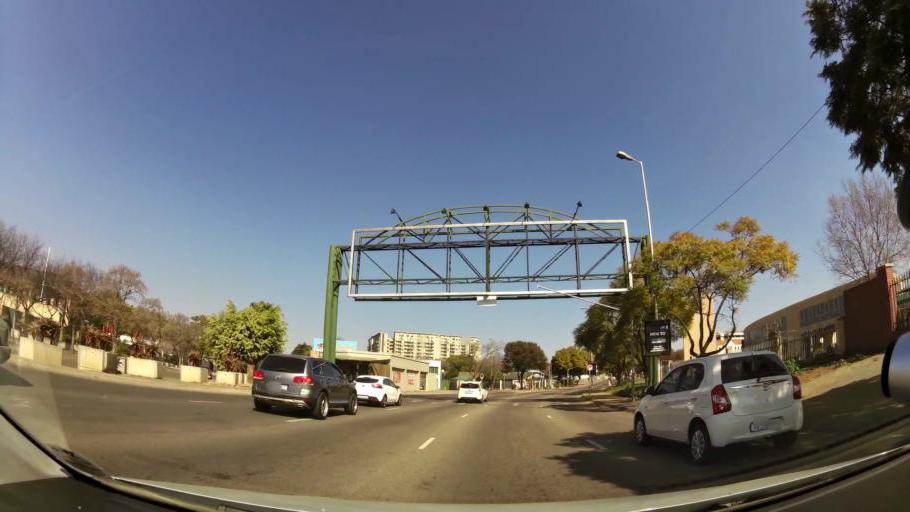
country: ZA
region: Gauteng
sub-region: City of Tshwane Metropolitan Municipality
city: Pretoria
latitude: -25.7449
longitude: 28.2420
